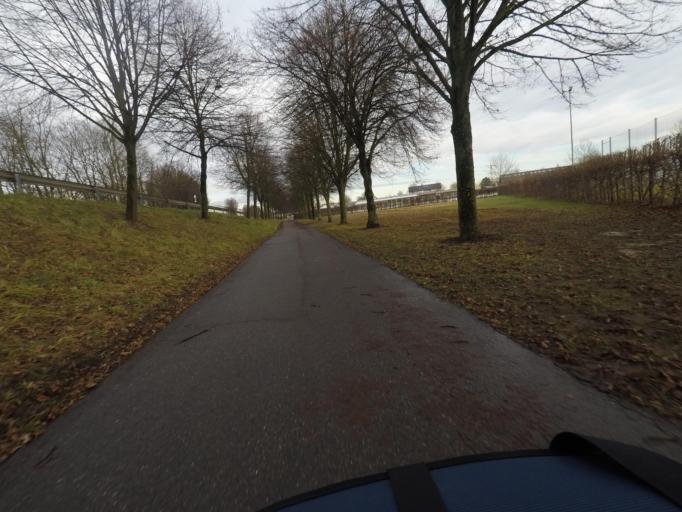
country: DE
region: Baden-Wuerttemberg
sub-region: Karlsruhe Region
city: Steinmauern
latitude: 48.8915
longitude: 8.1933
